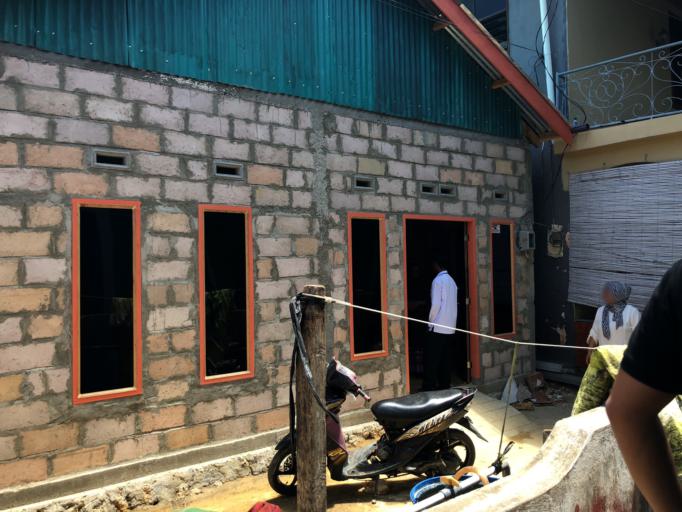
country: ID
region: Sulawesi Tenggara
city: Kendari
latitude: -3.9685
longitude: 122.5635
